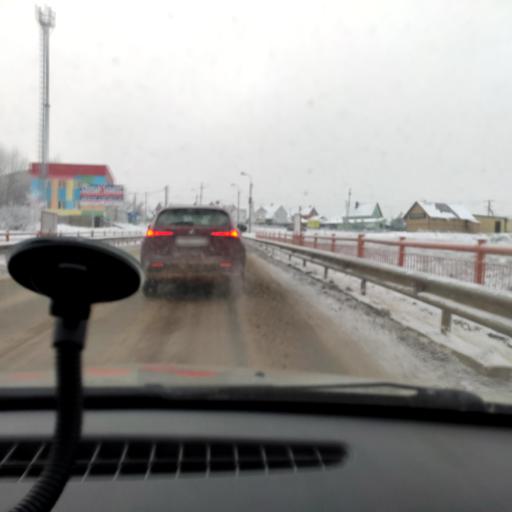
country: RU
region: Bashkortostan
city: Ufa
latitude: 54.6065
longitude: 55.9433
